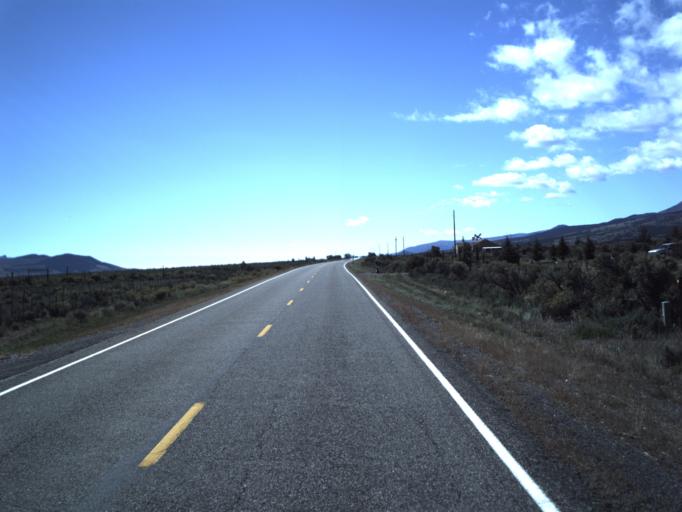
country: US
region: Utah
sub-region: Sevier County
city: Monroe
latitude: 38.4458
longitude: -111.9163
